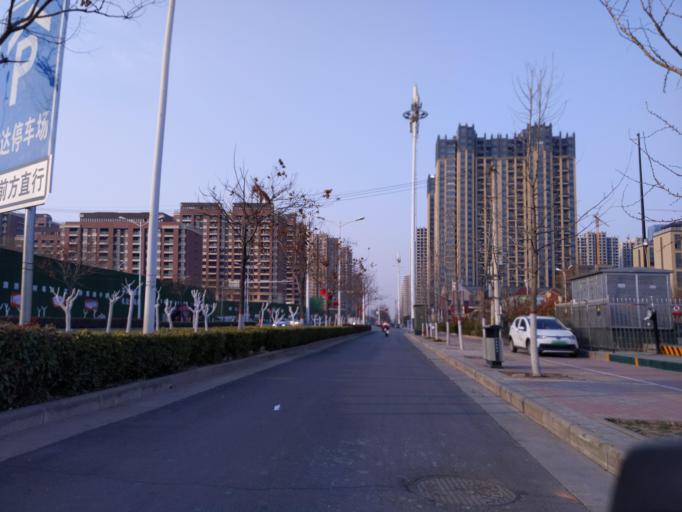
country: CN
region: Henan Sheng
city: Puyang
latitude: 35.7857
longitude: 115.0151
